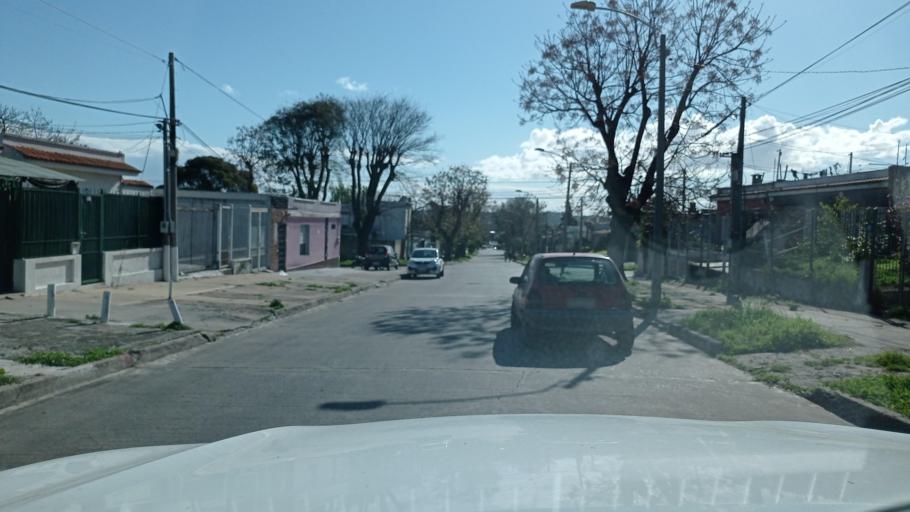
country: UY
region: Montevideo
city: Montevideo
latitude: -34.8517
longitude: -56.1750
